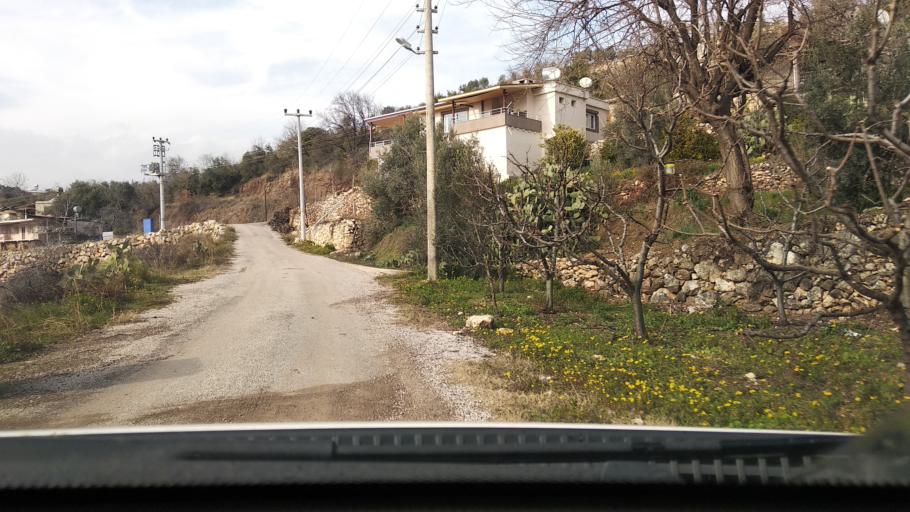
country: TR
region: Mersin
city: Kuzucubelen
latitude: 36.8772
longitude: 34.4686
